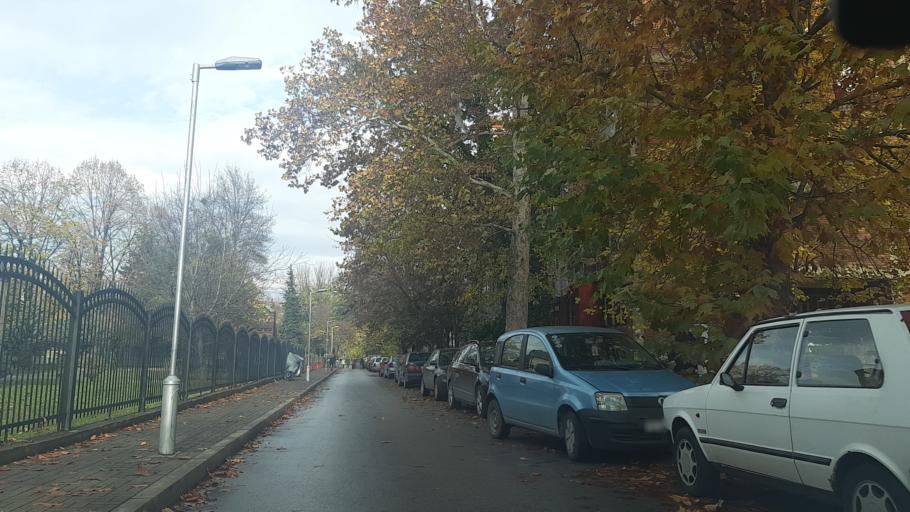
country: MK
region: Kisela Voda
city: Usje
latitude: 41.9854
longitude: 21.4582
